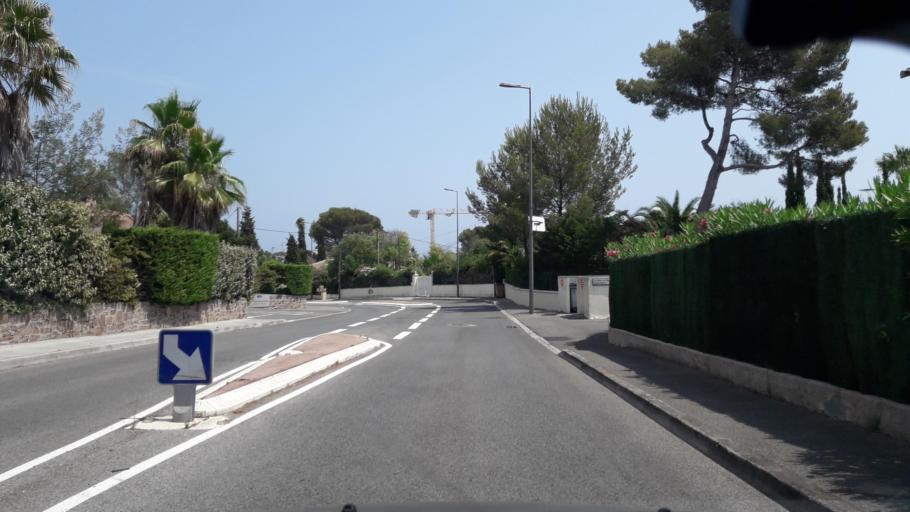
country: FR
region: Provence-Alpes-Cote d'Azur
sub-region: Departement du Var
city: Saint-Raphael
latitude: 43.4195
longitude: 6.7921
